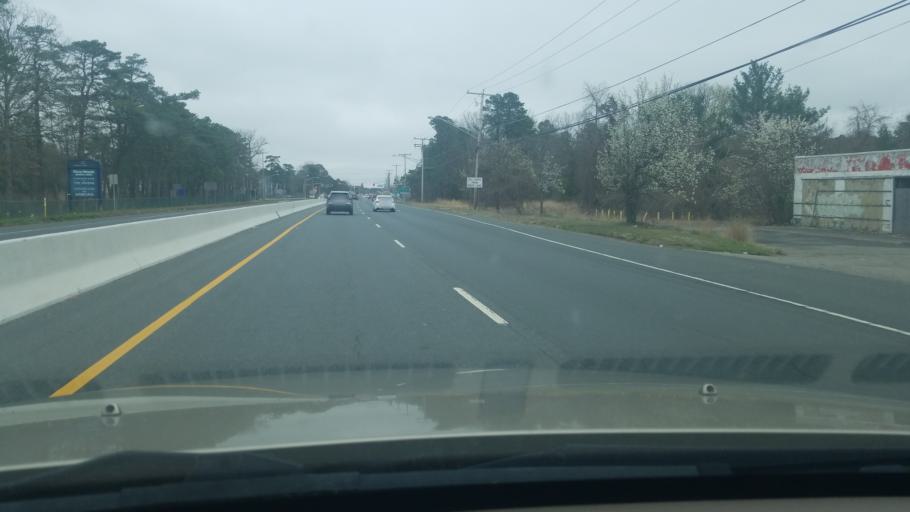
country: US
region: New Jersey
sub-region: Ocean County
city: Leisure Village West-Pine Lake Park
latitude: 39.9916
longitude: -74.2698
